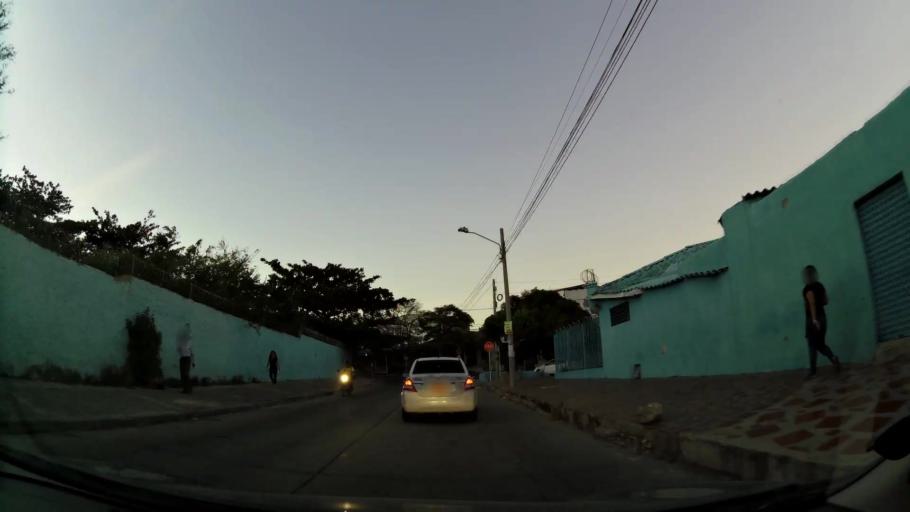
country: CO
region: Atlantico
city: Barranquilla
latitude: 10.9827
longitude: -74.8124
